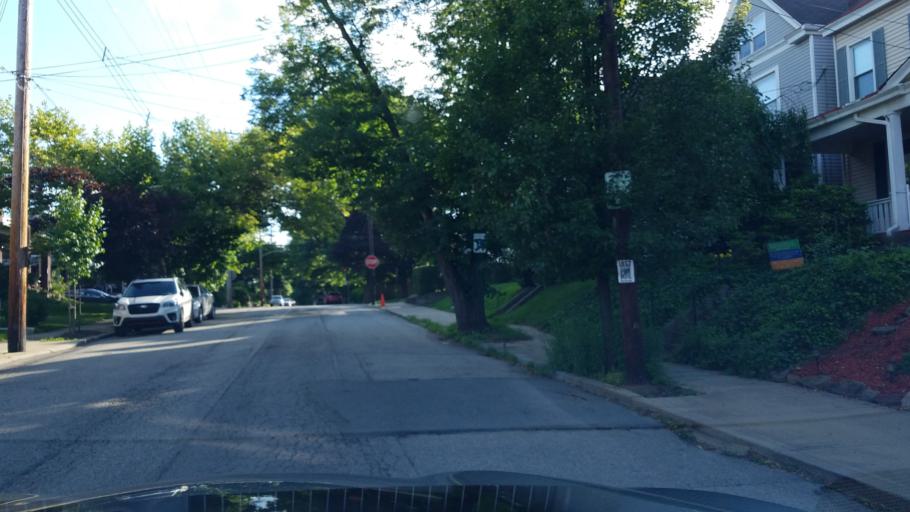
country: US
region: Pennsylvania
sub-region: Allegheny County
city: Swissvale
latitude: 40.4245
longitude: -79.8967
